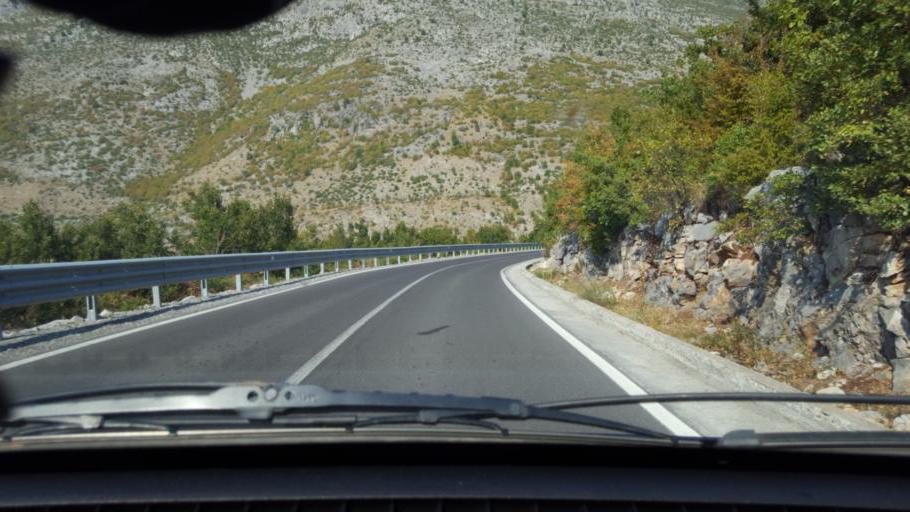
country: AL
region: Shkoder
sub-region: Rrethi i Malesia e Madhe
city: Hot
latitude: 42.3704
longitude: 19.4667
